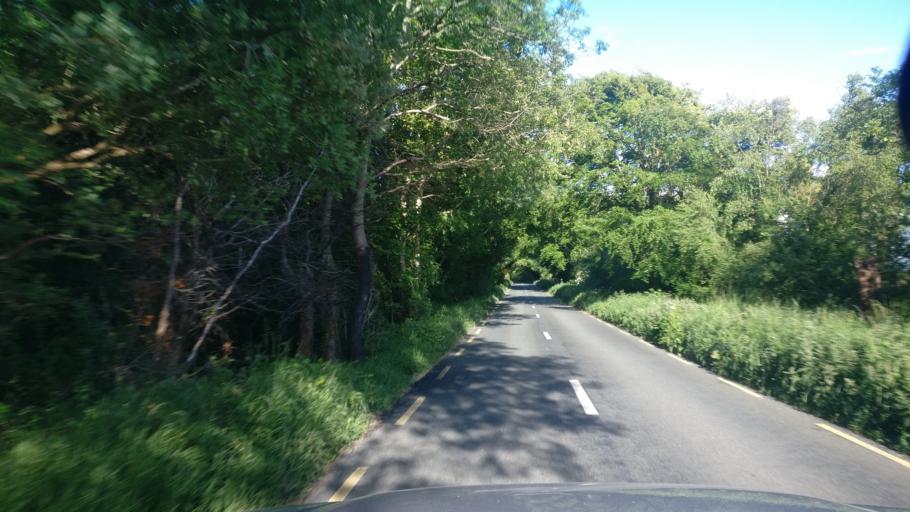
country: IE
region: Connaught
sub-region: County Galway
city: Ballinasloe
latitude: 53.2245
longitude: -8.2182
